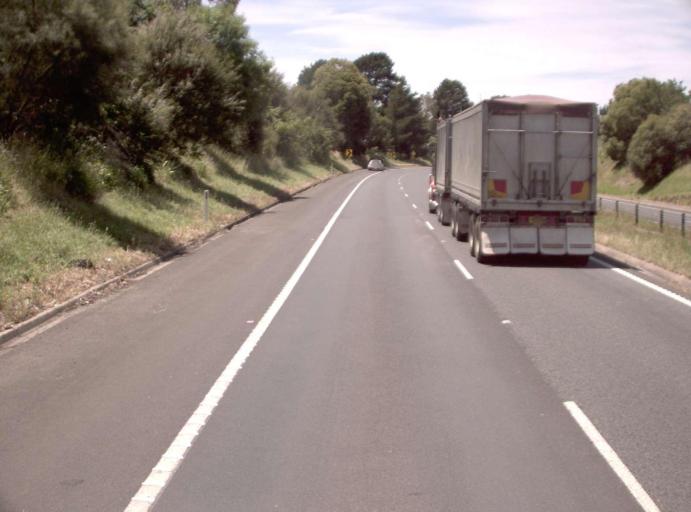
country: AU
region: Victoria
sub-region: Latrobe
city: Moe
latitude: -38.1827
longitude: 146.2674
